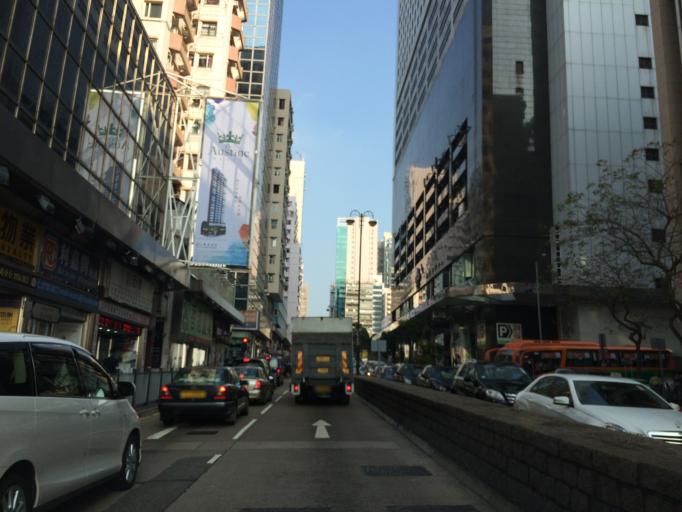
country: HK
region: Kowloon City
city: Kowloon
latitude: 22.3031
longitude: 114.1688
